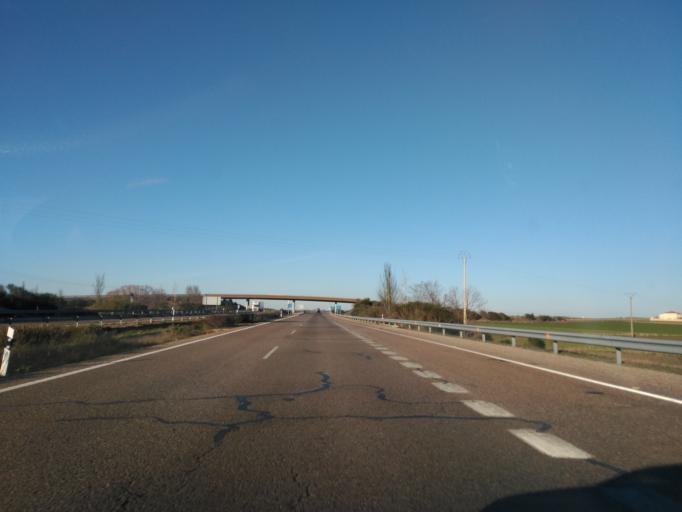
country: ES
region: Castille and Leon
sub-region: Provincia de Salamanca
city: Pedrosillo el Ralo
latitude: 41.0605
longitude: -5.5400
